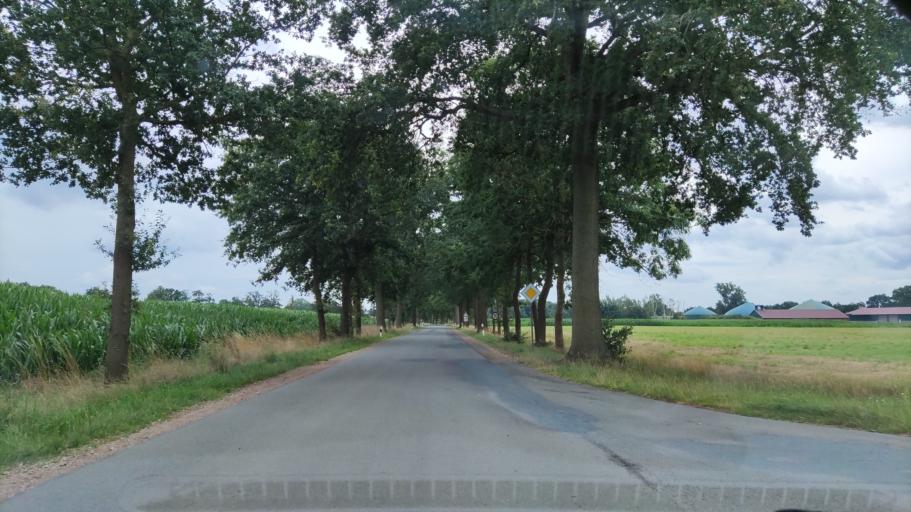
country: DE
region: Lower Saxony
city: Dannenberg
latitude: 53.0711
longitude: 11.1283
